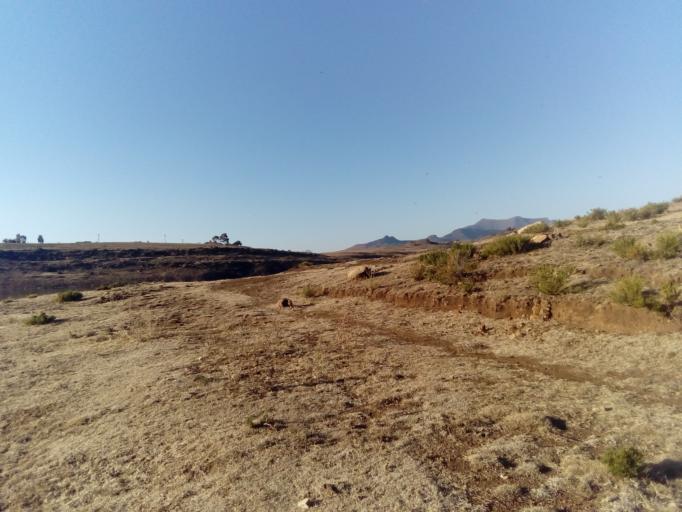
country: LS
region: Berea
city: Teyateyaneng
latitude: -29.3224
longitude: 27.8190
